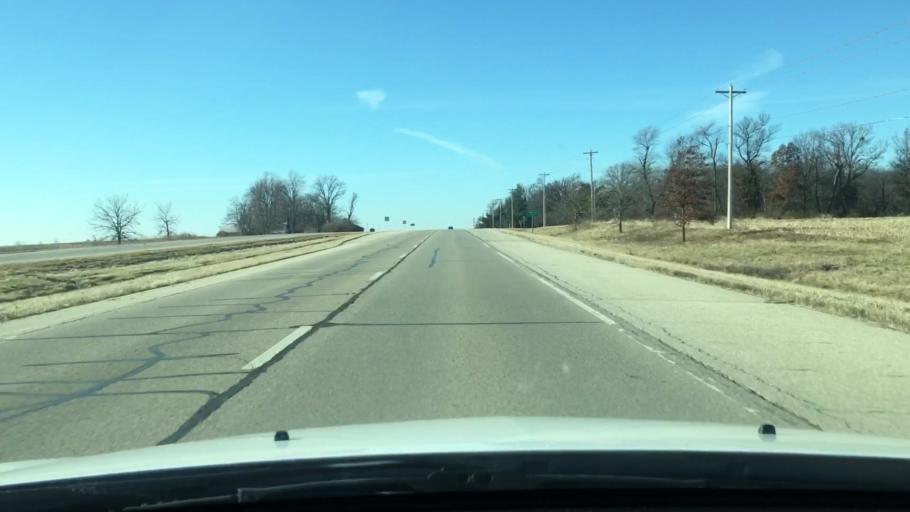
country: US
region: Illinois
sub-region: Woodford County
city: Metamora
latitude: 40.7800
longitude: -89.4065
